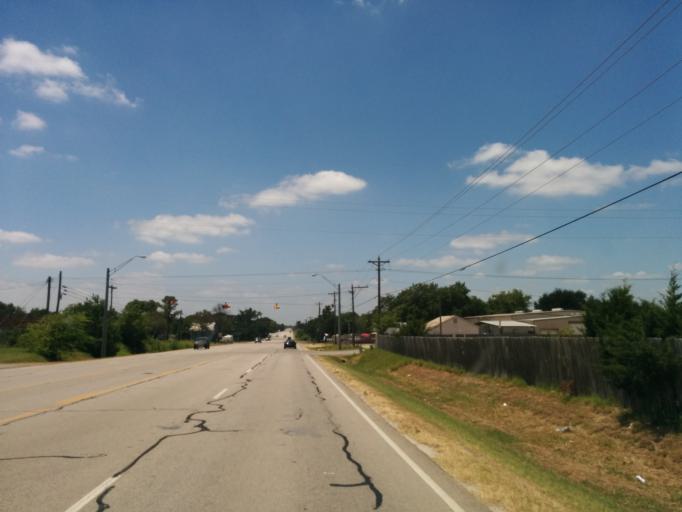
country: US
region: Texas
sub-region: Brazos County
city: Bryan
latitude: 30.7139
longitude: -96.3433
